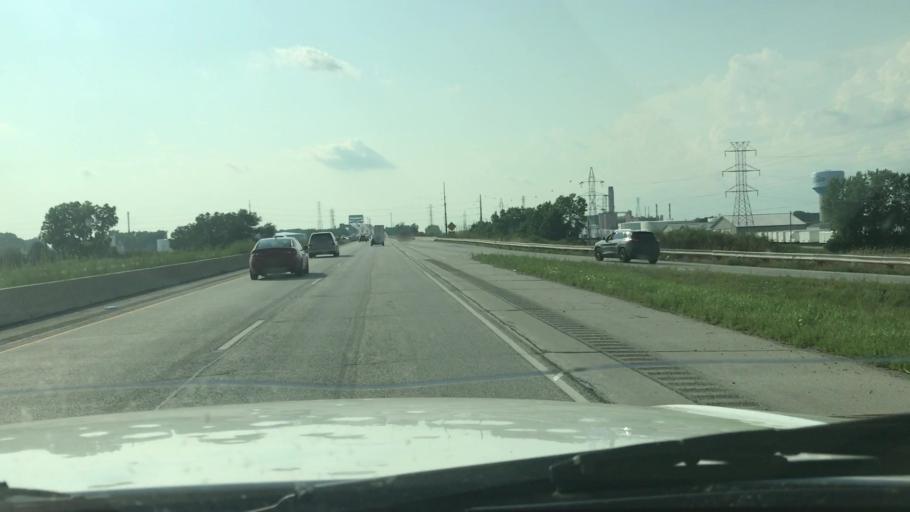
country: US
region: Wisconsin
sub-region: Brown County
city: Green Bay
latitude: 44.5267
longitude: -87.9868
